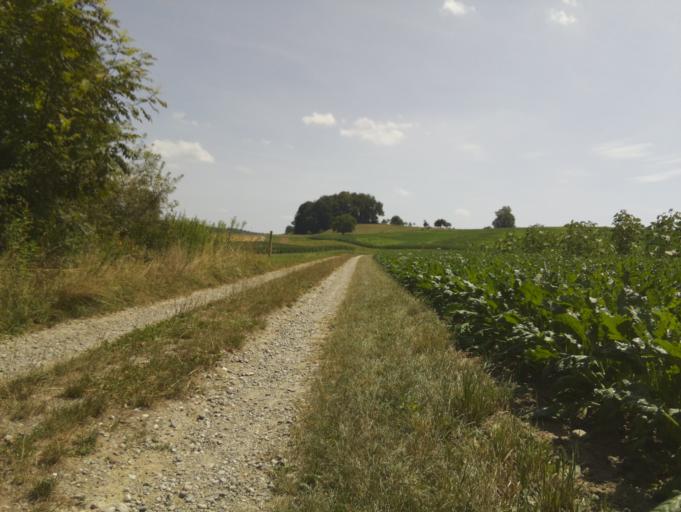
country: CH
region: Zurich
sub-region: Bezirk Andelfingen
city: Kleinandelfingen
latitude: 47.6188
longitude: 8.7151
